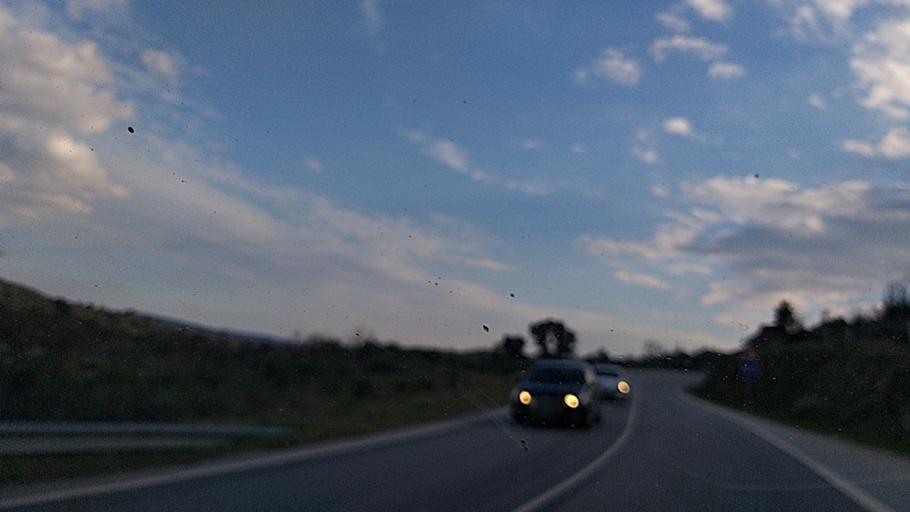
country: ES
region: Castille and Leon
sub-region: Provincia de Salamanca
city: Aldea del Obispo
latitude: 40.7024
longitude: -6.9325
